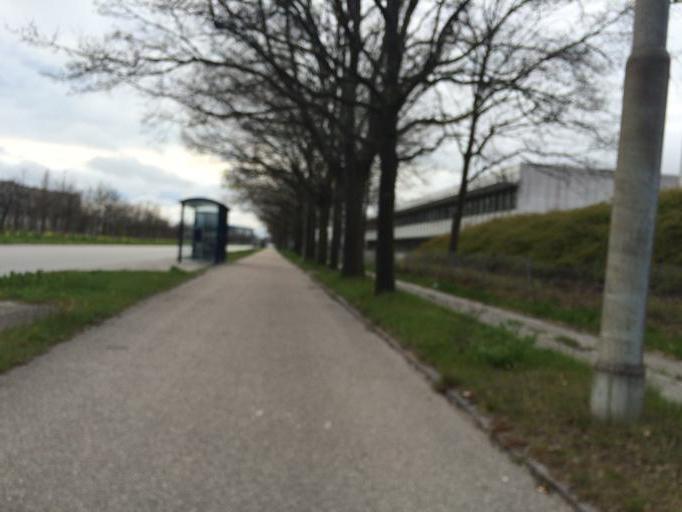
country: DK
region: Capital Region
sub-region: Hvidovre Kommune
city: Hvidovre
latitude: 55.6140
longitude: 12.4650
